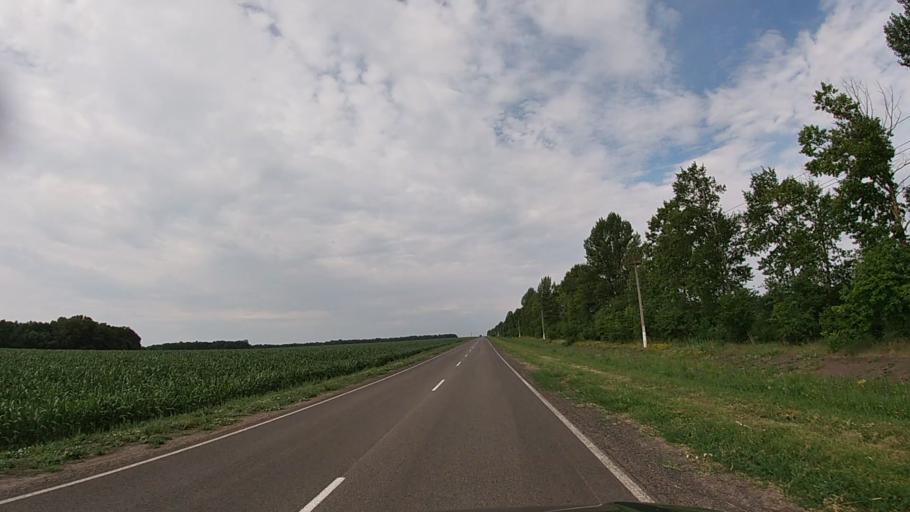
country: RU
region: Belgorod
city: Krasnaya Yaruga
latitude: 50.8277
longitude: 35.4728
